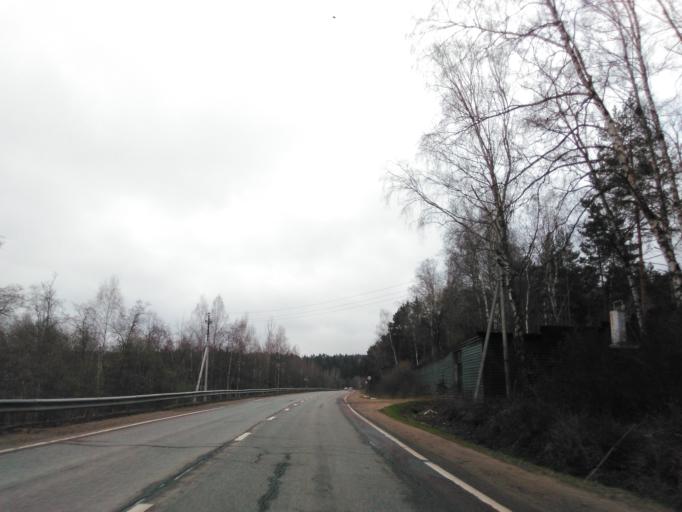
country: RU
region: Moskovskaya
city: Snegiri
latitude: 55.8469
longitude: 36.9573
